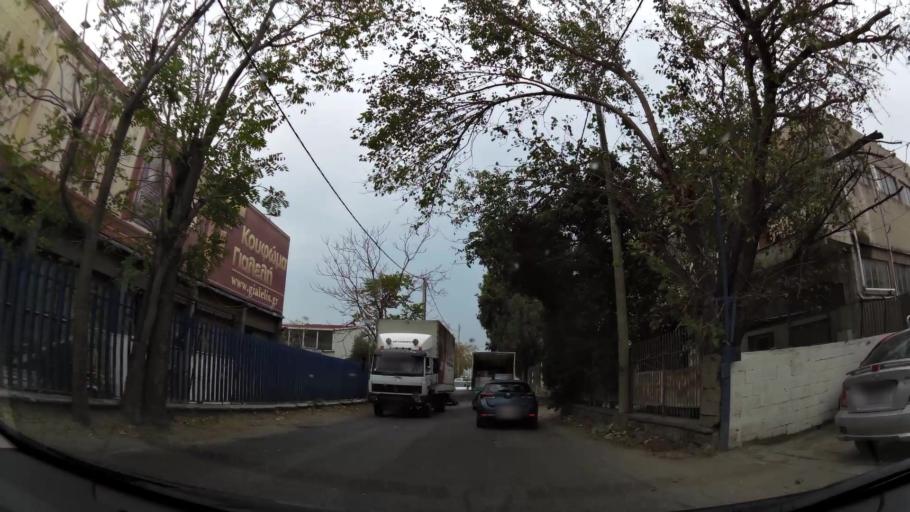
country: GR
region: Attica
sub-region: Nomarchia Athinas
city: Aigaleo
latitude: 37.9791
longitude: 23.6877
